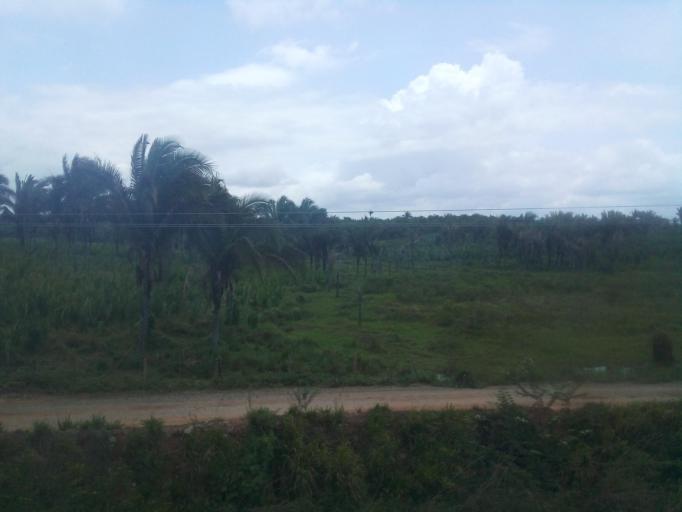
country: BR
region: Maranhao
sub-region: Santa Ines
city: Santa Ines
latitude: -3.7202
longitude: -45.5174
